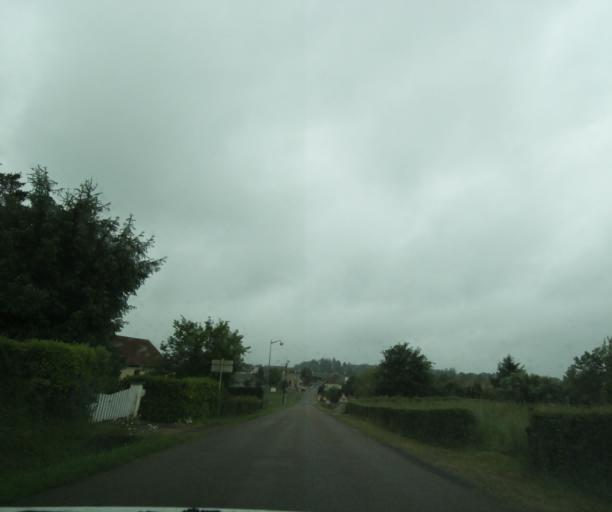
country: FR
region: Bourgogne
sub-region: Departement de Saone-et-Loire
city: Palinges
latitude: 46.4957
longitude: 4.2145
